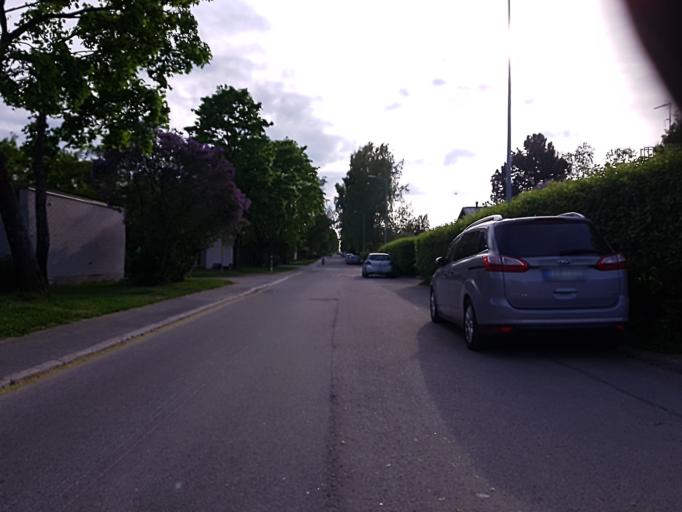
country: FI
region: Uusimaa
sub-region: Helsinki
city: Helsinki
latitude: 60.2386
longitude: 24.9430
